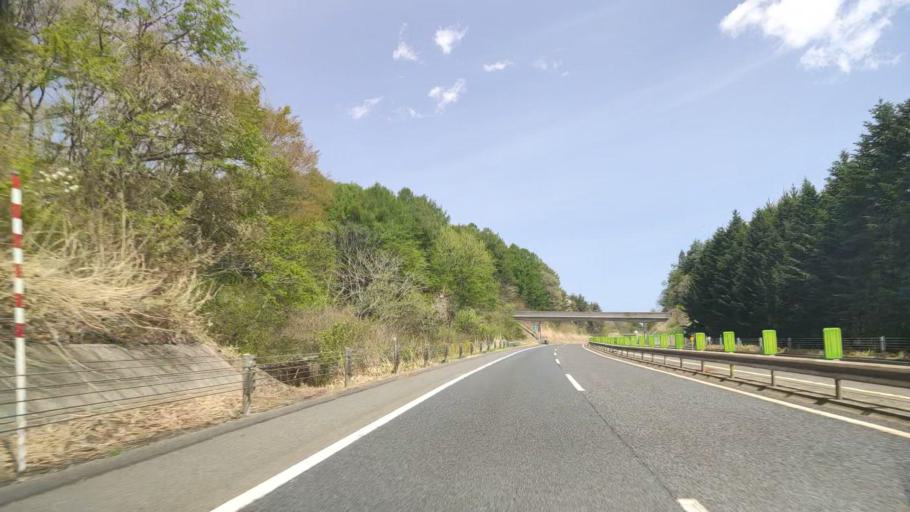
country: JP
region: Aomori
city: Hachinohe
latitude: 40.4277
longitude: 141.4401
